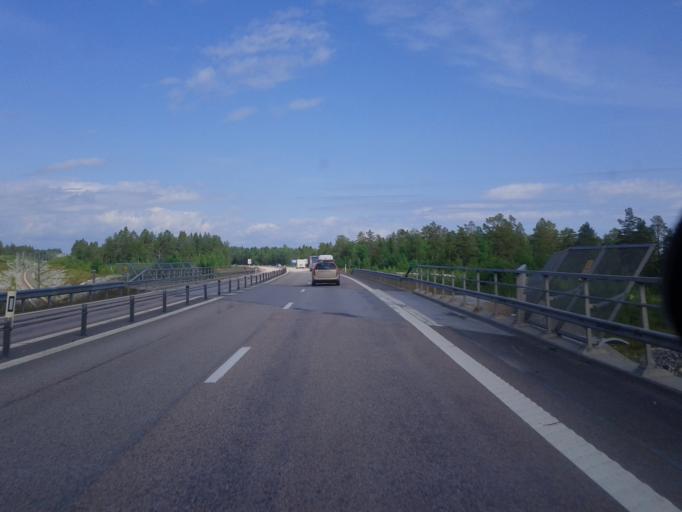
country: SE
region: Vaesternorrland
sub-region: OErnskoeldsviks Kommun
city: Husum
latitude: 63.3681
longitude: 19.1870
